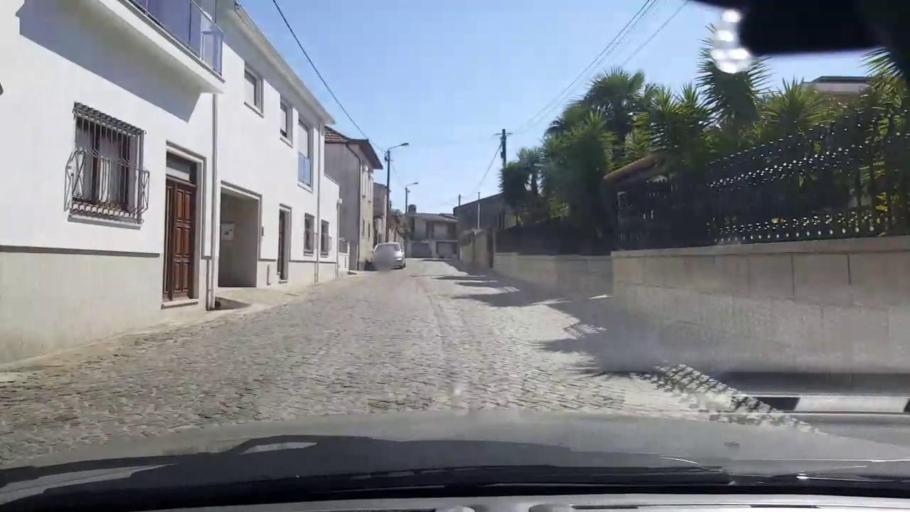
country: PT
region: Porto
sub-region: Matosinhos
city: Lavra
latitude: 41.2958
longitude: -8.7246
